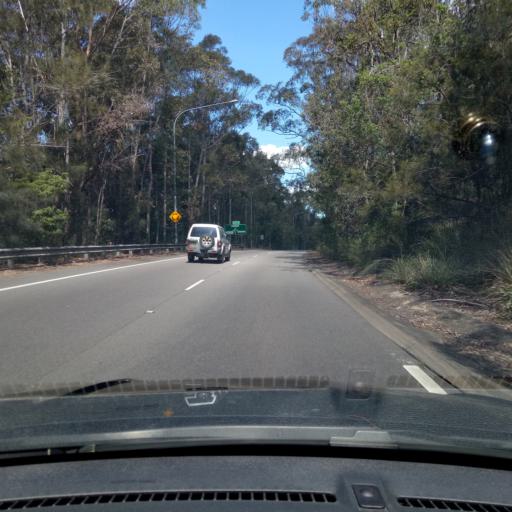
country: AU
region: New South Wales
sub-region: Wyong Shire
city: Chittaway Bay
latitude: -33.3342
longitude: 151.4317
